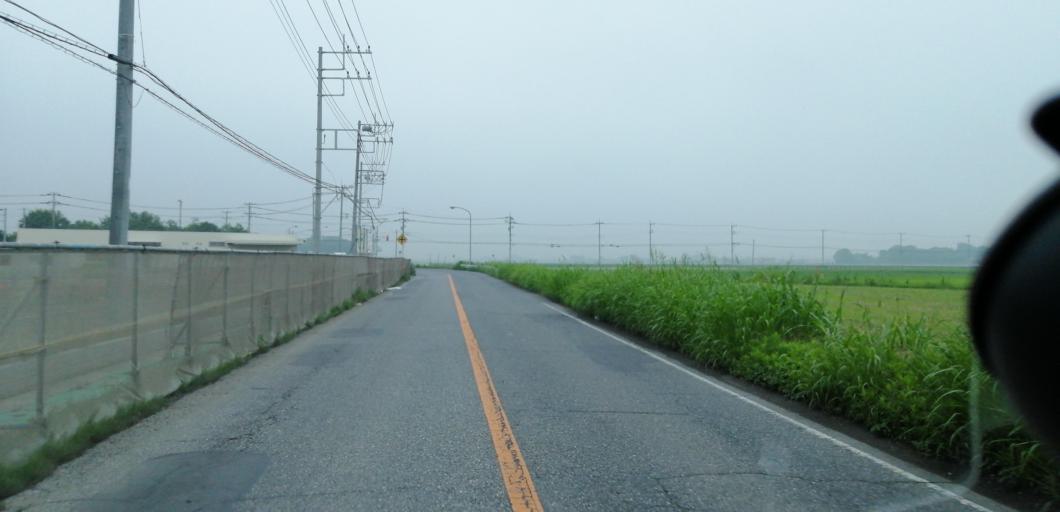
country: JP
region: Chiba
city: Noda
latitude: 36.0002
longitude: 139.8581
